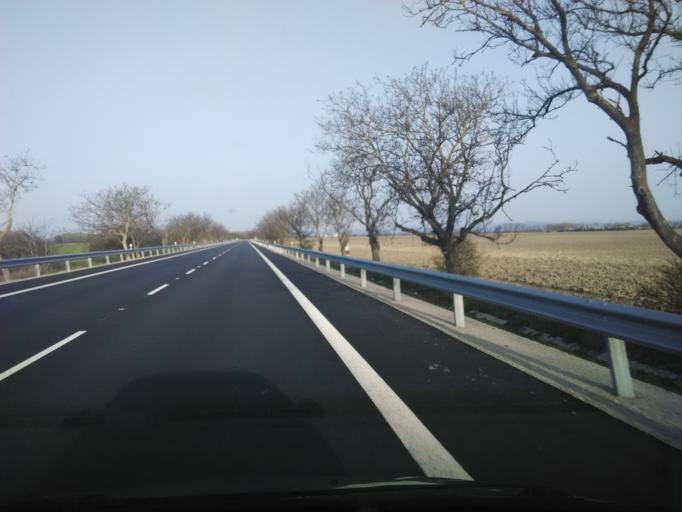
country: SK
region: Trnavsky
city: Sladkovicovo
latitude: 48.1966
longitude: 17.5822
